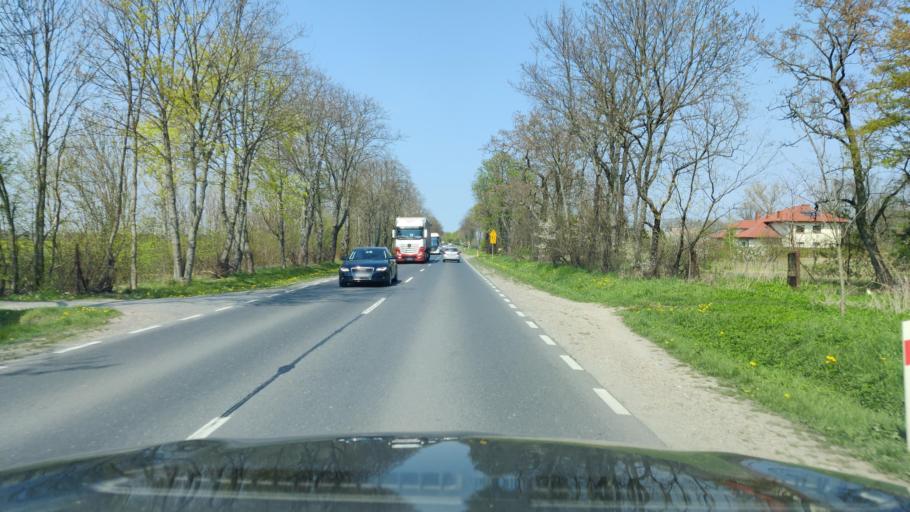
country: PL
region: Masovian Voivodeship
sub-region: Powiat pultuski
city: Pultusk
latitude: 52.6395
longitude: 21.0936
